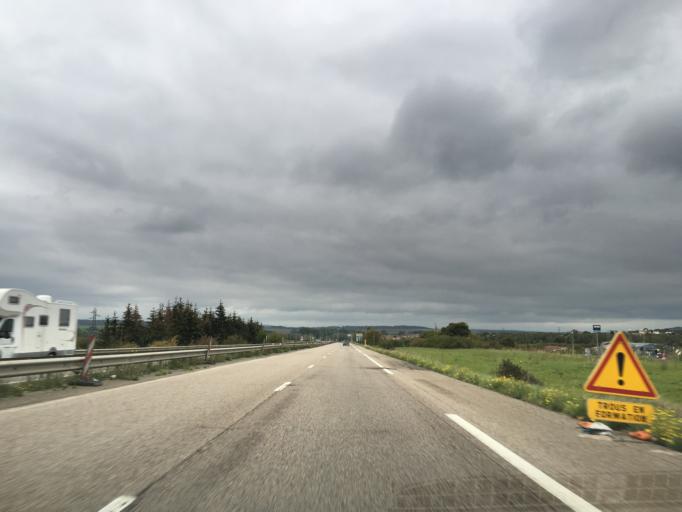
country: FR
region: Lorraine
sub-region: Departement de Meurthe-et-Moselle
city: Foug
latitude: 48.6829
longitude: 5.7368
